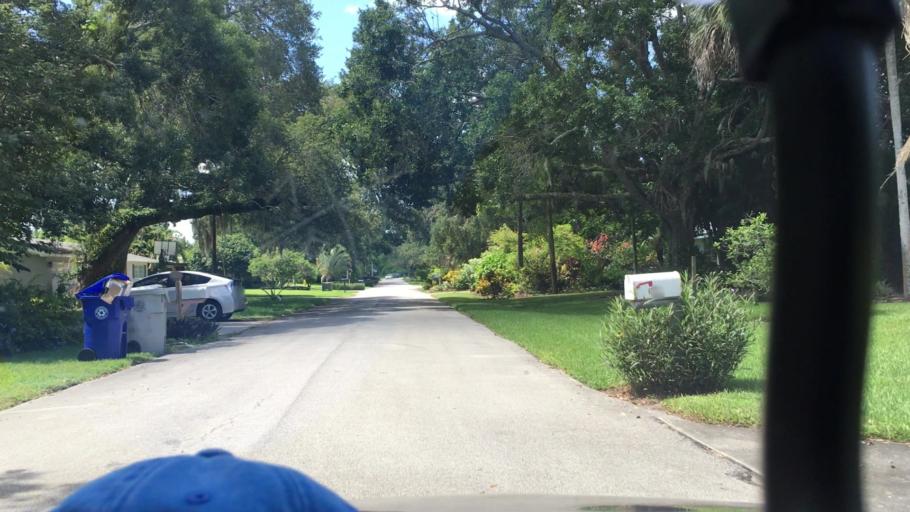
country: US
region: Florida
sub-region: Indian River County
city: Vero Beach
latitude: 27.6527
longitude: -80.3950
